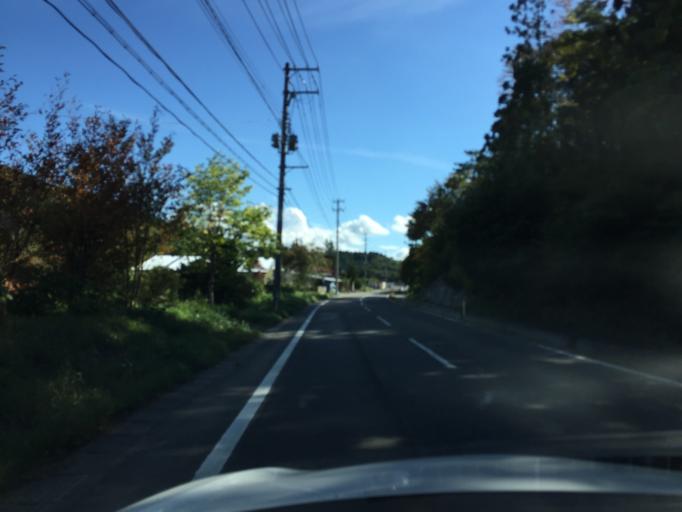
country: JP
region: Fukushima
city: Ishikawa
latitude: 37.2285
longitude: 140.5673
